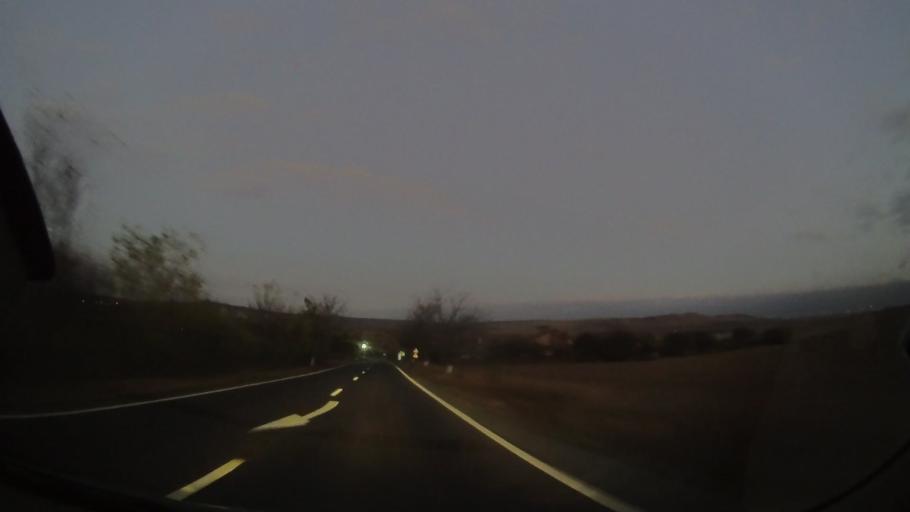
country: RO
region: Tulcea
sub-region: Comuna Frecatei
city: Cataloi
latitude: 45.0872
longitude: 28.7186
